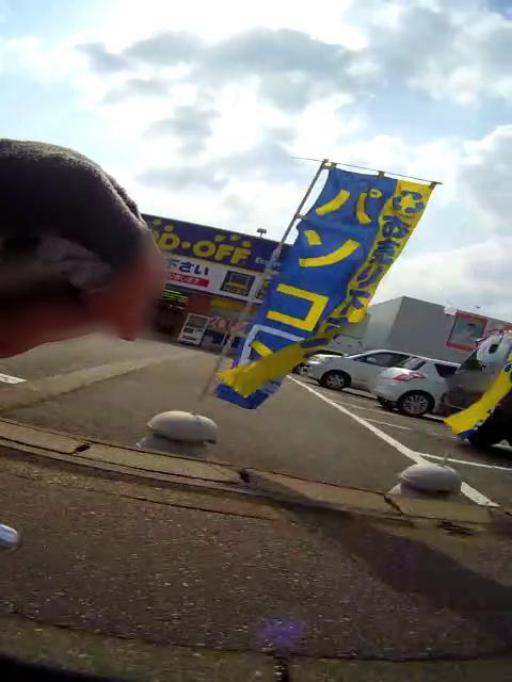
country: JP
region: Toyama
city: Takaoka
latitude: 36.7331
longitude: 137.0029
